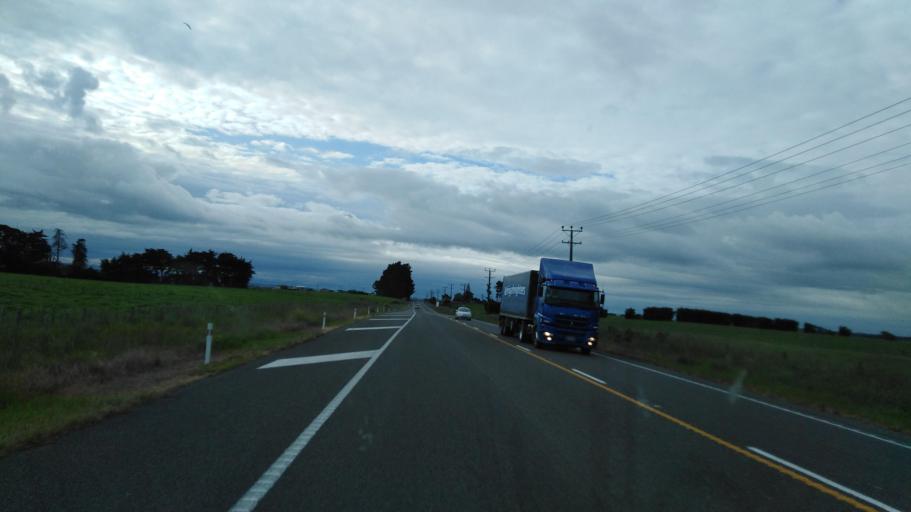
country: NZ
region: Manawatu-Wanganui
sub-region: Rangitikei District
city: Bulls
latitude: -40.1363
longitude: 175.3643
